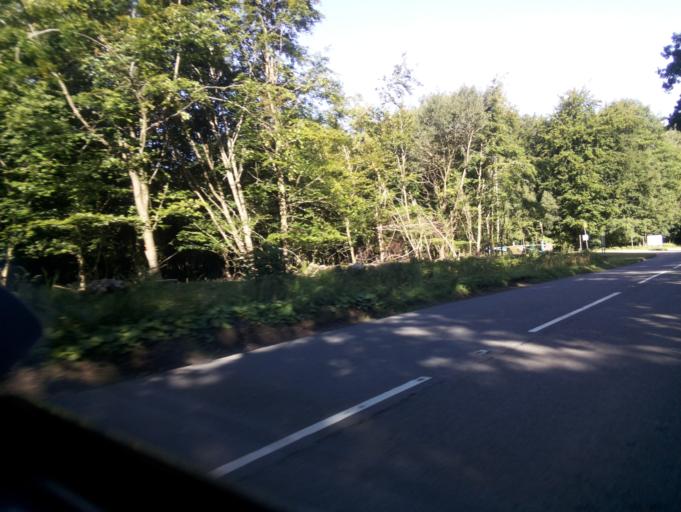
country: GB
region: England
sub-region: Gloucestershire
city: Coleford
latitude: 51.8024
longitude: -2.6361
